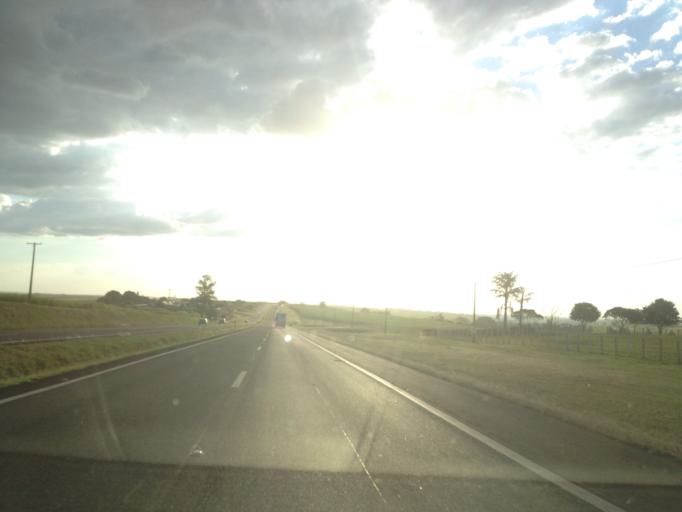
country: BR
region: Sao Paulo
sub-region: Jau
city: Jau
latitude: -22.2709
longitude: -48.4749
